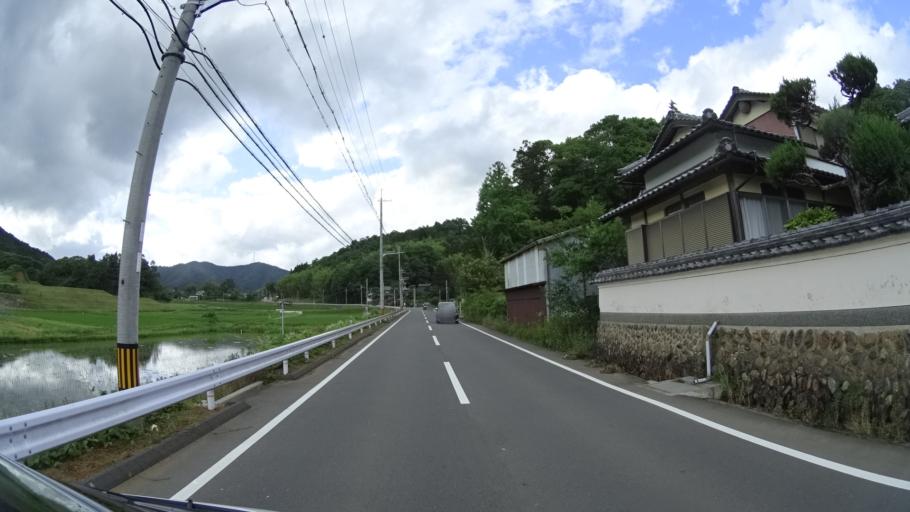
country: JP
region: Kyoto
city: Ayabe
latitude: 35.3367
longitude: 135.2039
